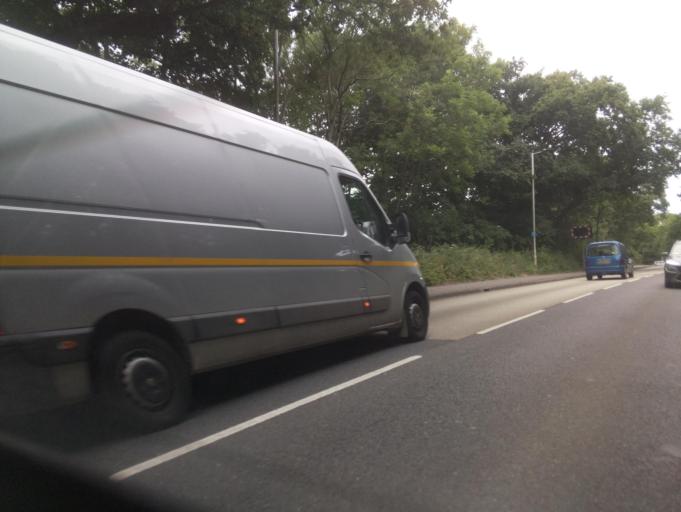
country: GB
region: England
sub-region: Devon
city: Heavitree
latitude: 50.7165
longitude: -3.4748
